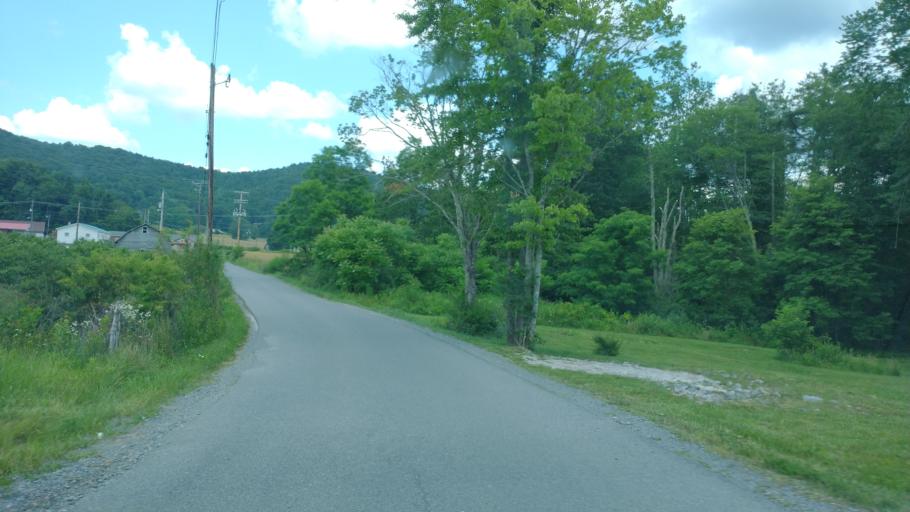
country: US
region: West Virginia
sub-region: Mercer County
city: Athens
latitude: 37.4563
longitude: -81.0130
